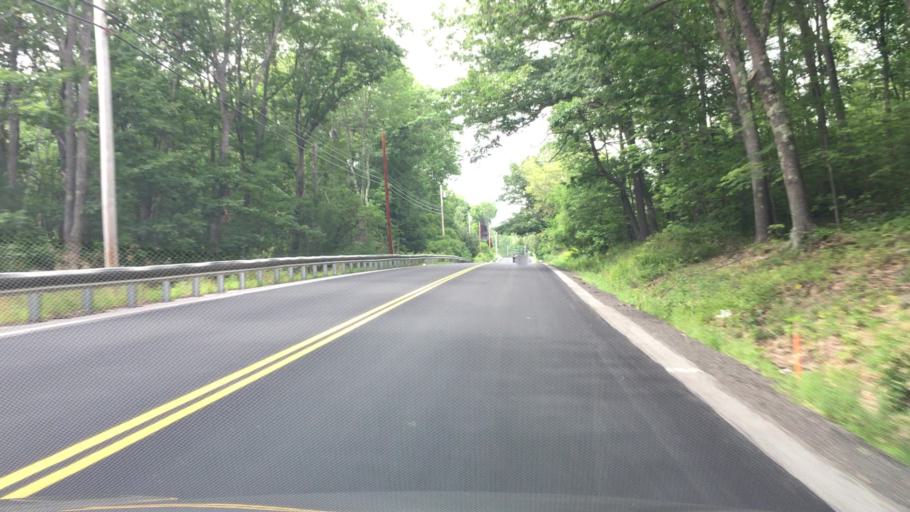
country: US
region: Maine
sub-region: Waldo County
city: Winterport
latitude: 44.6132
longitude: -68.8246
